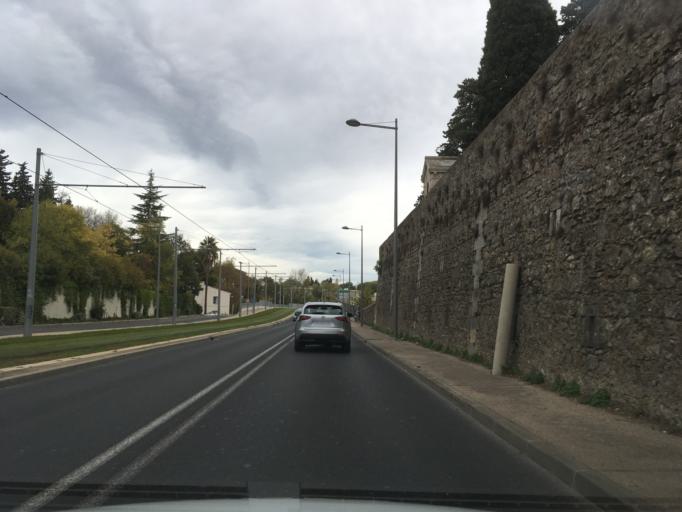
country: FR
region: Languedoc-Roussillon
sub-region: Departement de l'Herault
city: Castelnau-le-Lez
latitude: 43.6277
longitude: 3.8925
